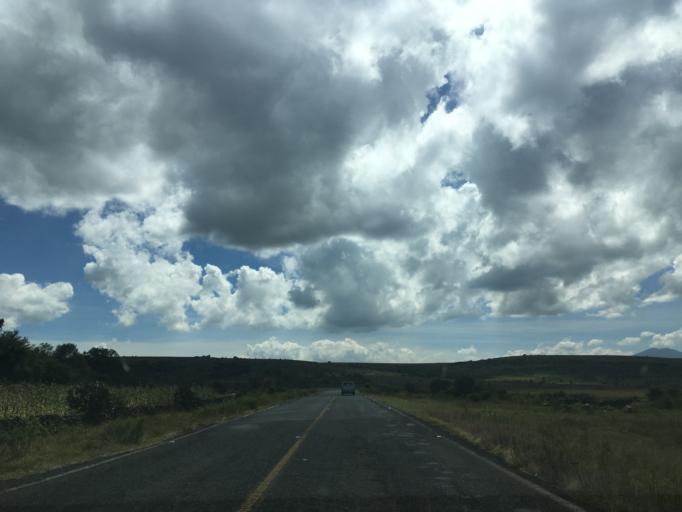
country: MX
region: Michoacan
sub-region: Morelia
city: Cuto de la Esperanza
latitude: 19.7736
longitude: -101.3960
